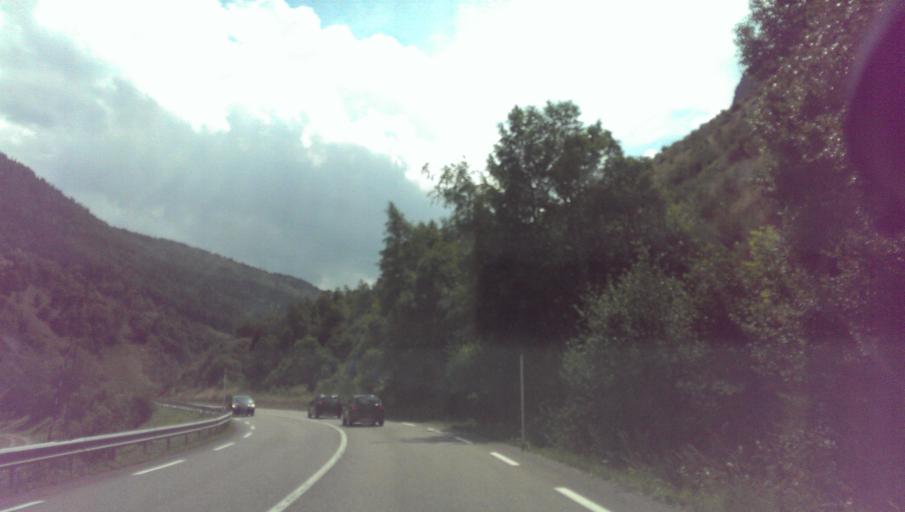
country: AD
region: Encamp
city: Pas de la Casa
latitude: 42.5865
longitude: 1.7958
